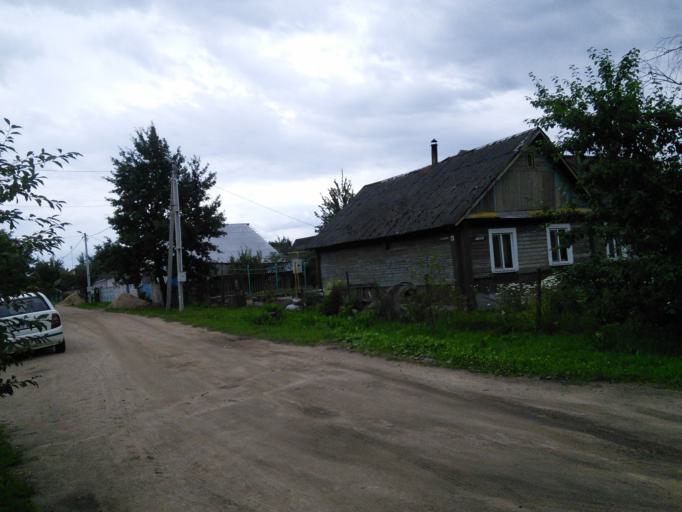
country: BY
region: Minsk
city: Maladzyechna
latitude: 54.3122
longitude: 26.8625
